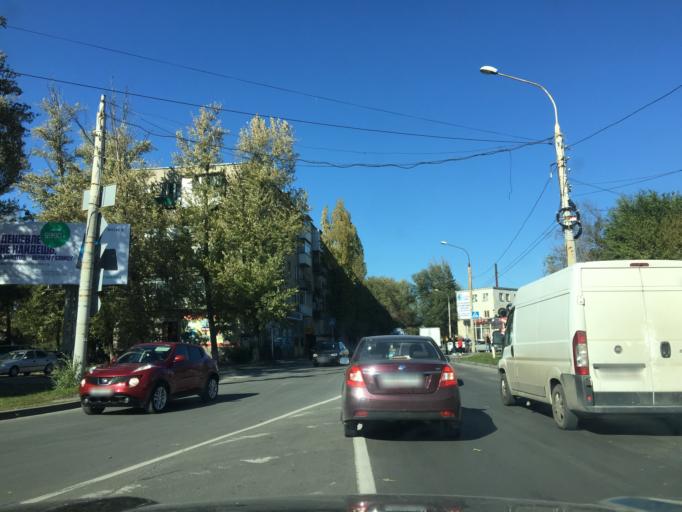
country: RU
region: Rostov
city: Imeni Chkalova
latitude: 47.2497
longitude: 39.7567
